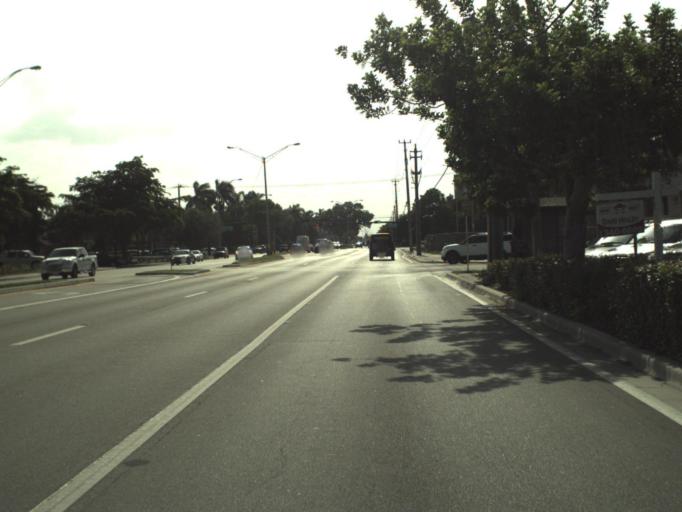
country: US
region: Florida
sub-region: Broward County
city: Coral Springs
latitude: 26.2727
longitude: -80.2644
